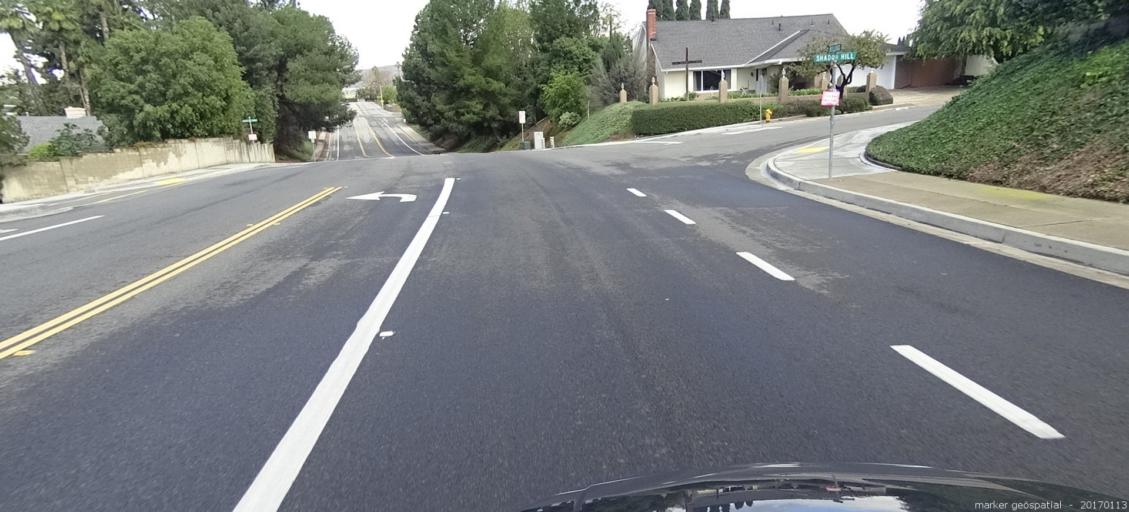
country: US
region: California
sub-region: Orange County
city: Yorba Linda
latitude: 33.8847
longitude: -117.7957
